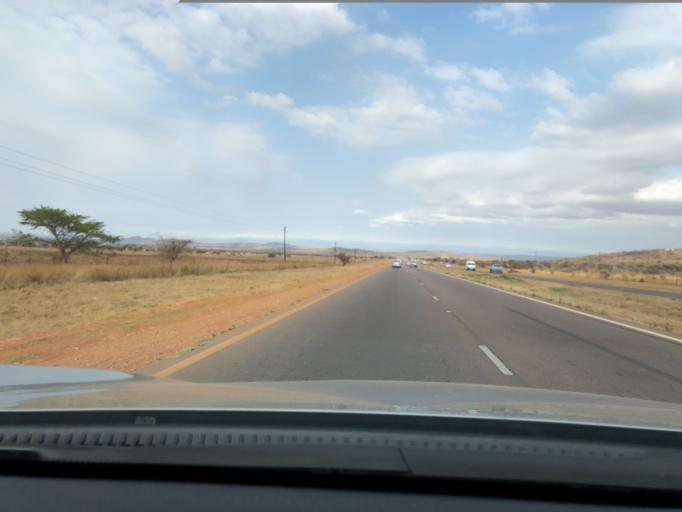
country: ZA
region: Limpopo
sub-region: Capricorn District Municipality
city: Polokwane
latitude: -23.8991
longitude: 29.5453
